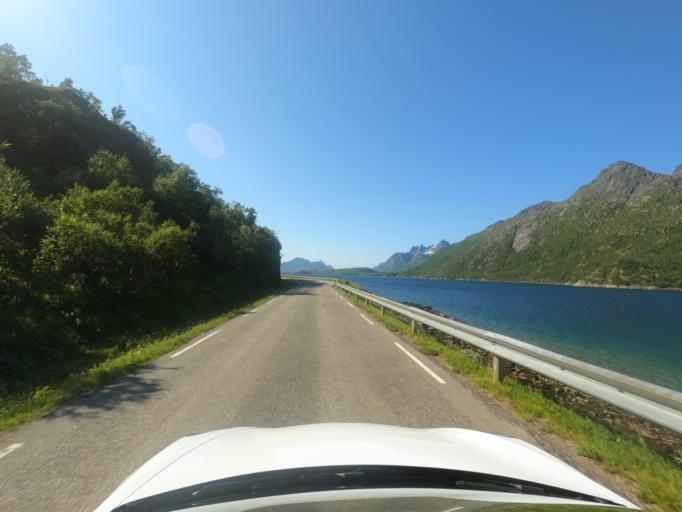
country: NO
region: Nordland
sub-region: Hadsel
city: Stokmarknes
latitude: 68.3851
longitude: 15.0908
